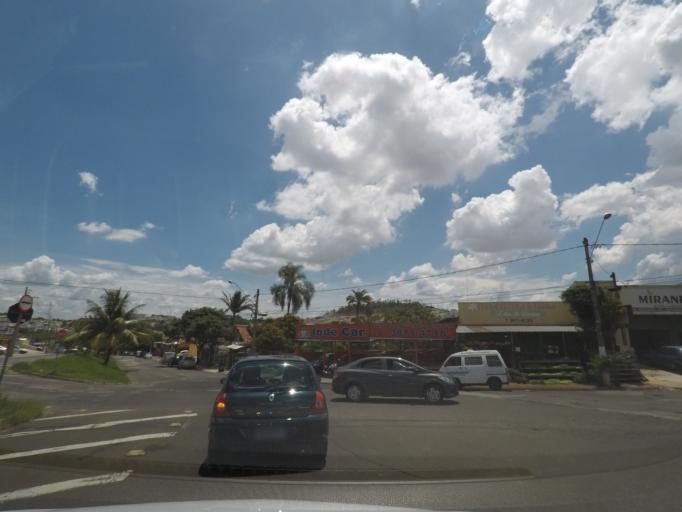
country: BR
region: Sao Paulo
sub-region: Valinhos
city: Valinhos
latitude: -22.9444
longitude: -46.9961
